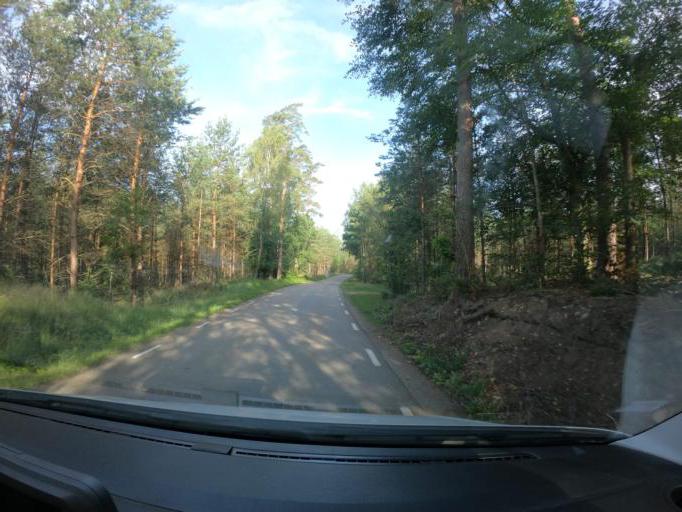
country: SE
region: Skane
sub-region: Angelholms Kommun
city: Munka-Ljungby
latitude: 56.3102
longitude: 13.0613
